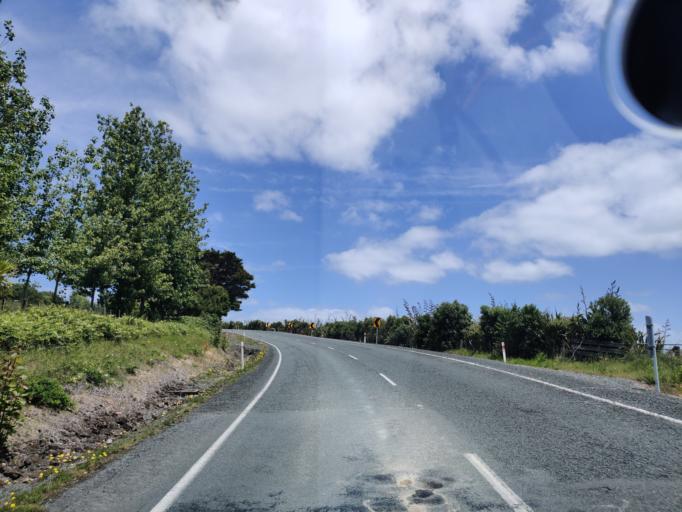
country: NZ
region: Auckland
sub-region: Auckland
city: Wellsford
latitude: -36.3809
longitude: 174.4491
